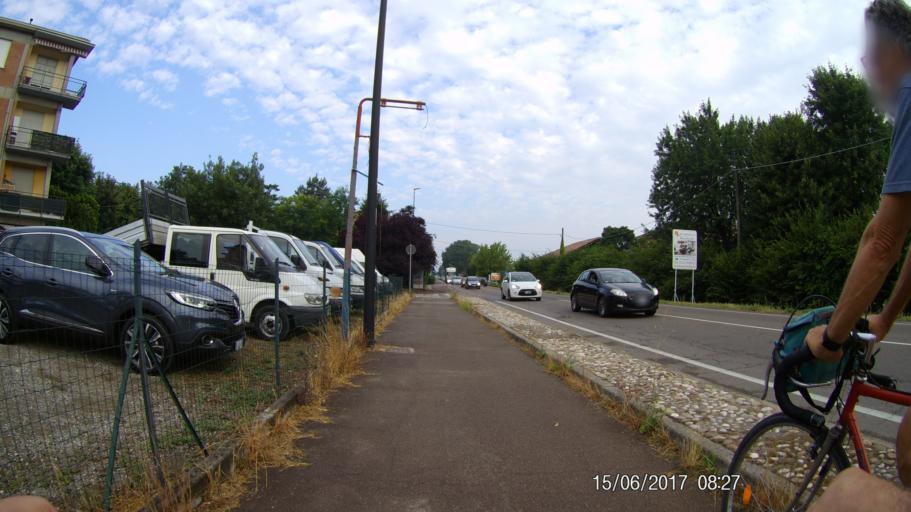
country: IT
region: Emilia-Romagna
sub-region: Provincia di Reggio Emilia
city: Roncocesi
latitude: 44.7251
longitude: 10.5545
